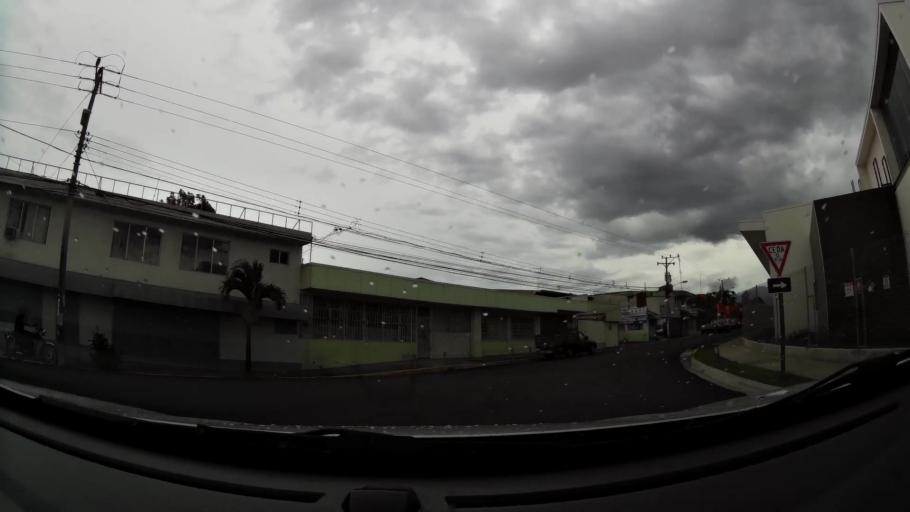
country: CR
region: San Jose
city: San Juan
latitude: 9.9587
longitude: -84.0782
